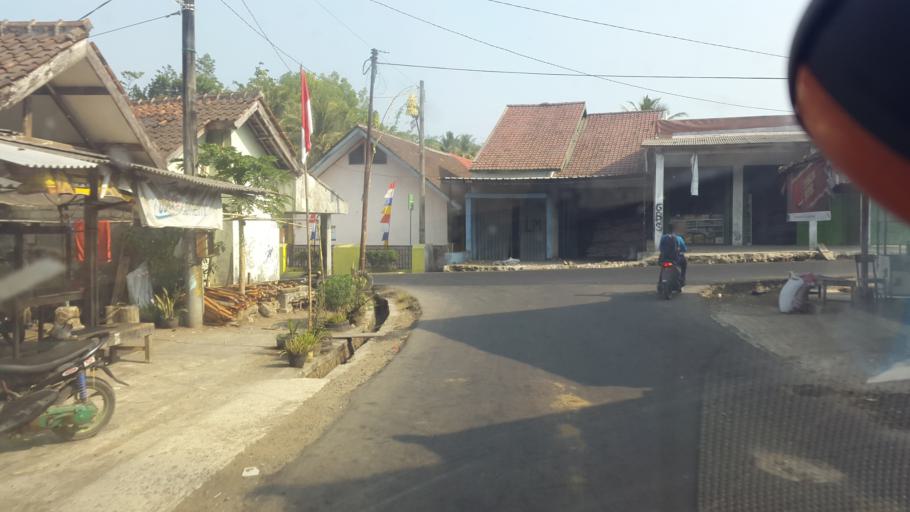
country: ID
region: West Java
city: Karadenan
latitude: -7.3481
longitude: 106.6164
